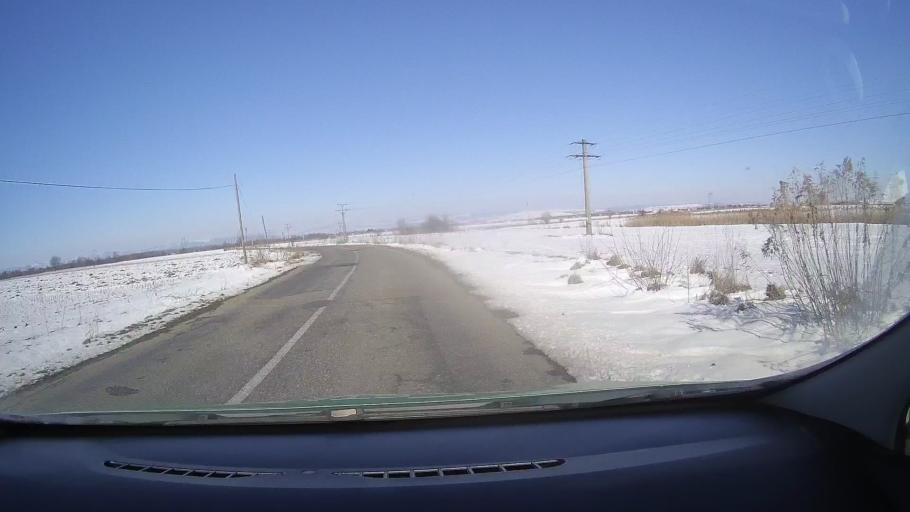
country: RO
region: Brasov
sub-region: Comuna Harseni
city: Harseni
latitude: 45.7674
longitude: 25.0039
